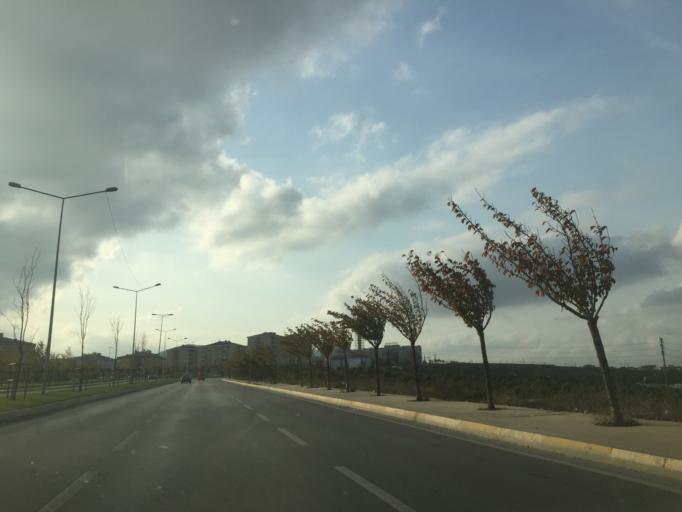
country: TR
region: Istanbul
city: Sultanbeyli
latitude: 40.9400
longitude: 29.3122
